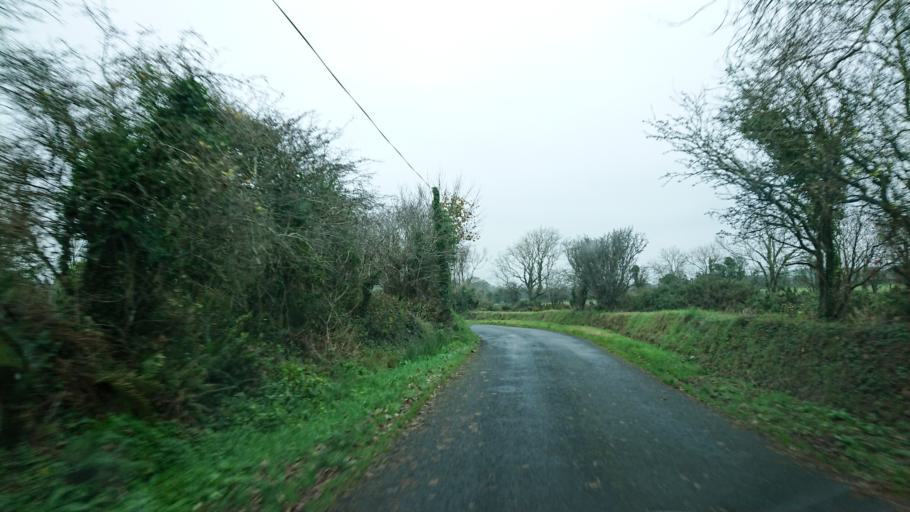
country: IE
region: Munster
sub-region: Waterford
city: Dunmore East
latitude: 52.1744
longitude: -7.0166
